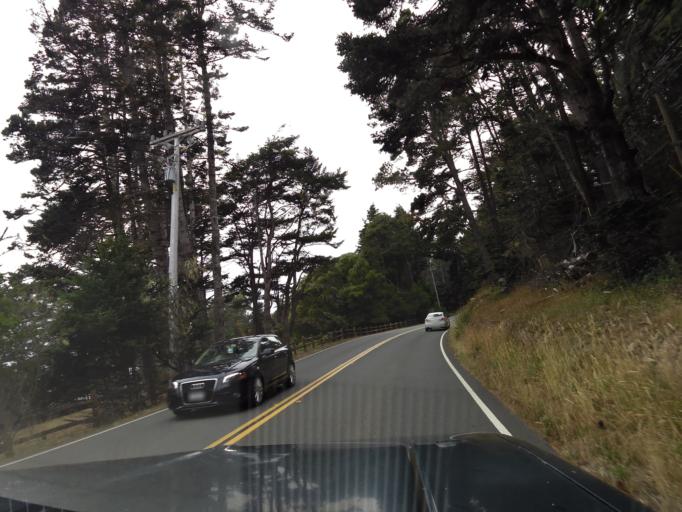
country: US
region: California
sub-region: Mendocino County
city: Fort Bragg
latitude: 39.2409
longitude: -123.7729
